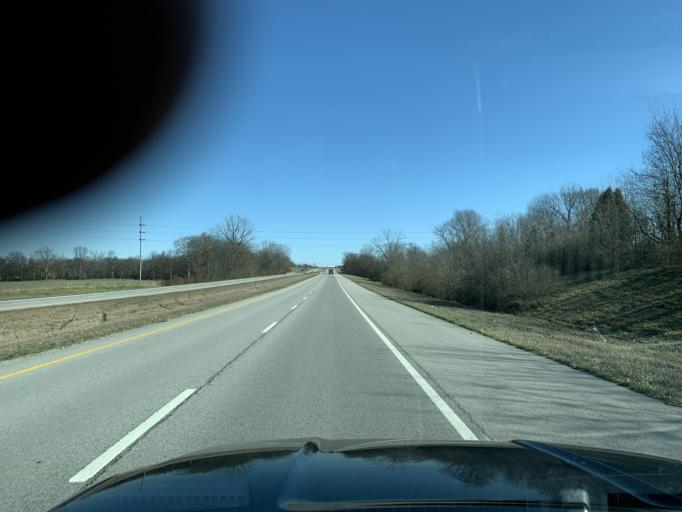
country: US
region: Tennessee
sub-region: Maury County
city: Mount Pleasant
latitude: 35.5541
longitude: -87.2015
